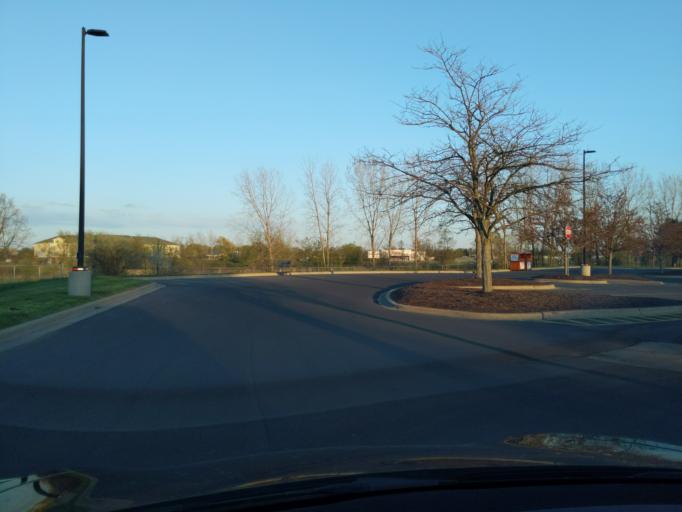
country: US
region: Michigan
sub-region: Jackson County
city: Jackson
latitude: 42.2683
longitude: -84.4597
